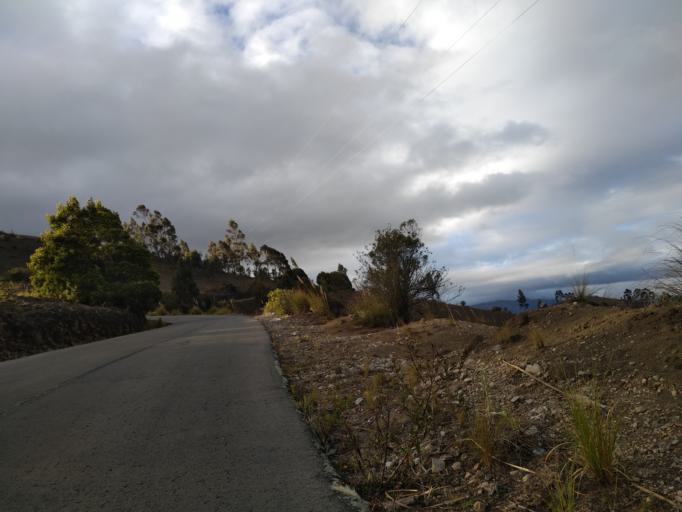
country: EC
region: Chimborazo
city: Riobamba
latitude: -1.7018
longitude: -78.7090
